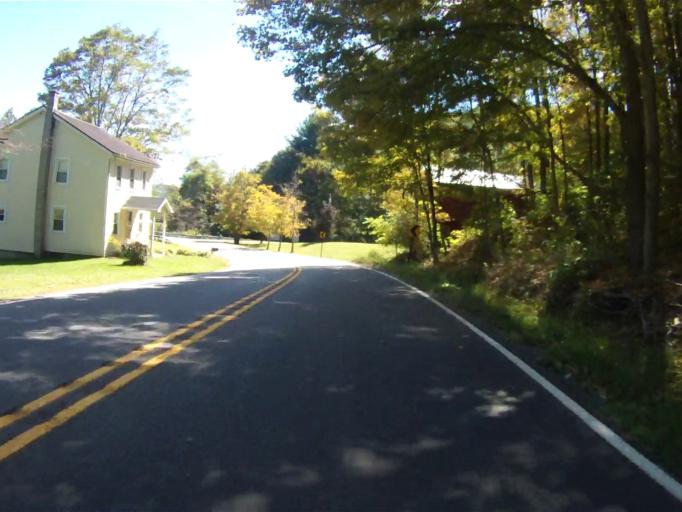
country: US
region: Pennsylvania
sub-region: Centre County
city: Milesburg
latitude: 40.9241
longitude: -77.9009
